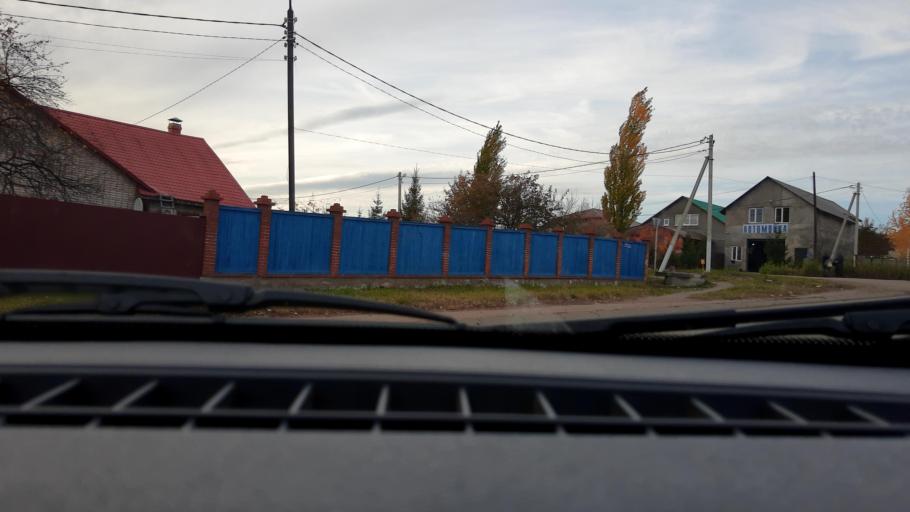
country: RU
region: Bashkortostan
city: Mikhaylovka
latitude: 54.8078
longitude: 55.8891
